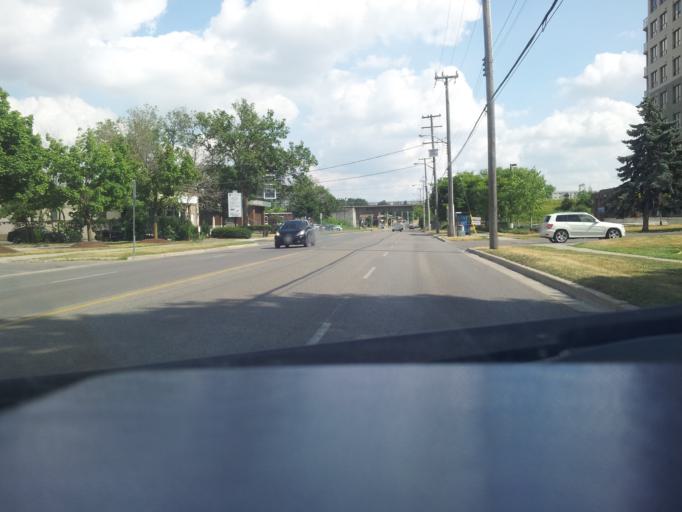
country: CA
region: Ontario
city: Waterloo
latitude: 43.4499
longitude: -80.5158
